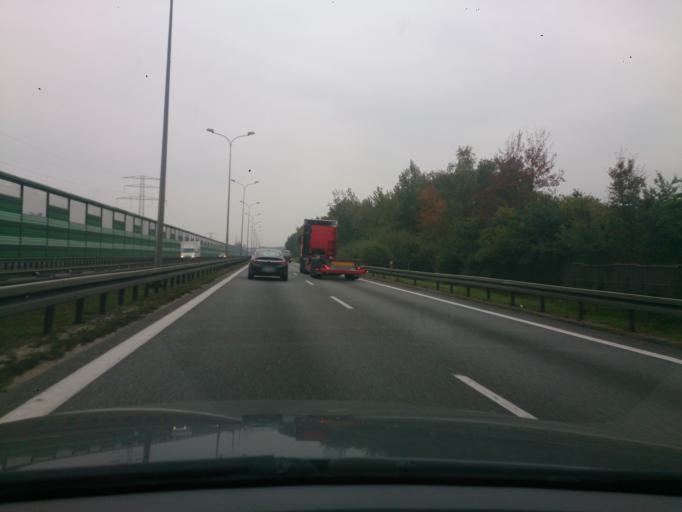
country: PL
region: Pomeranian Voivodeship
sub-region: Gdynia
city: Wielki Kack
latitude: 54.4174
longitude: 18.4871
